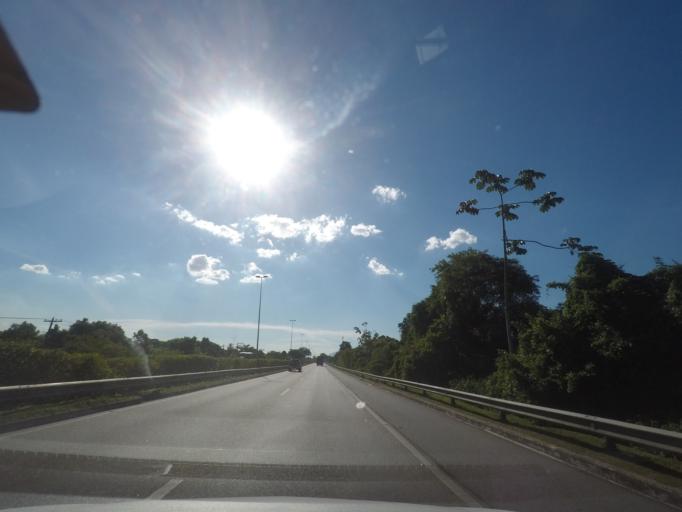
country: BR
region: Rio de Janeiro
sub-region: Petropolis
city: Petropolis
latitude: -22.6466
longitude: -43.1977
